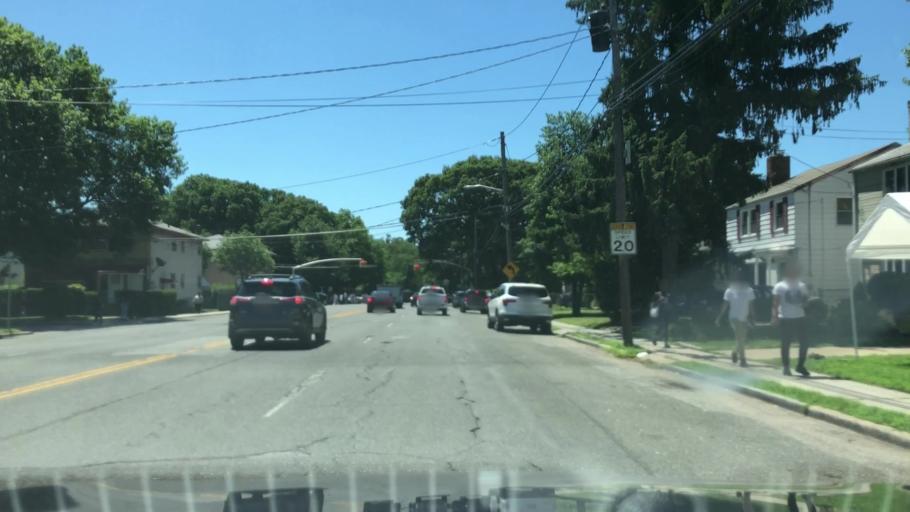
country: US
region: New York
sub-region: Nassau County
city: Hempstead
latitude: 40.6995
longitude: -73.6311
